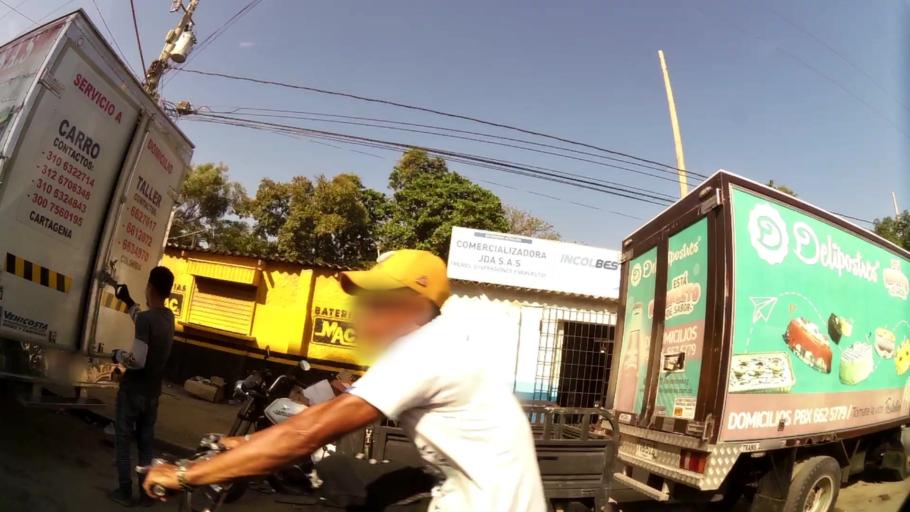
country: CO
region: Bolivar
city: Cartagena
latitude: 10.3892
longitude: -75.5215
